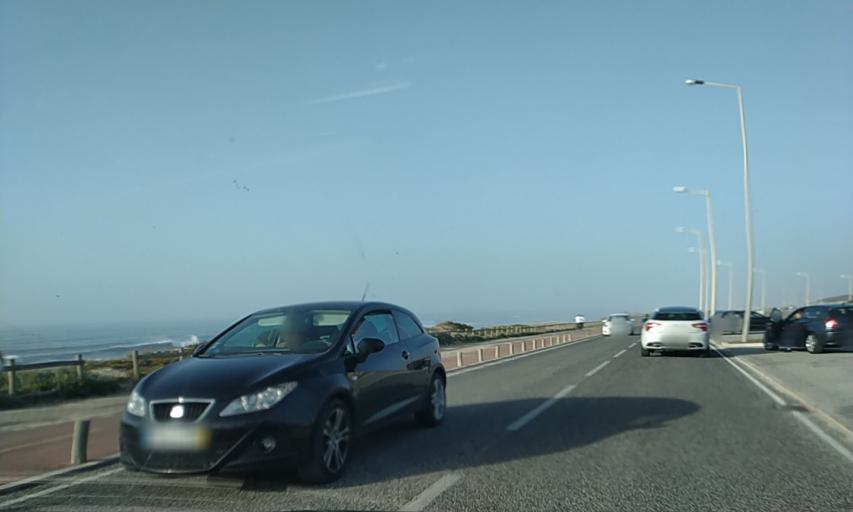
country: PT
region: Leiria
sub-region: Marinha Grande
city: Marinha Grande
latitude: 39.7656
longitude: -9.0301
